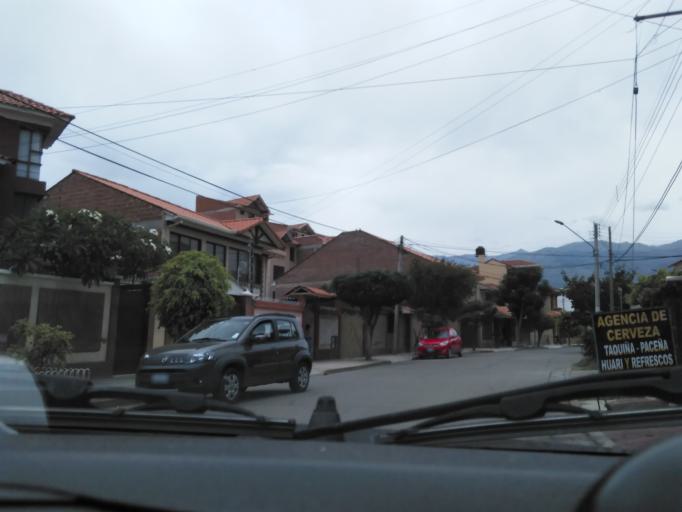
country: BO
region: Cochabamba
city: Cochabamba
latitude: -17.3903
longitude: -66.1849
